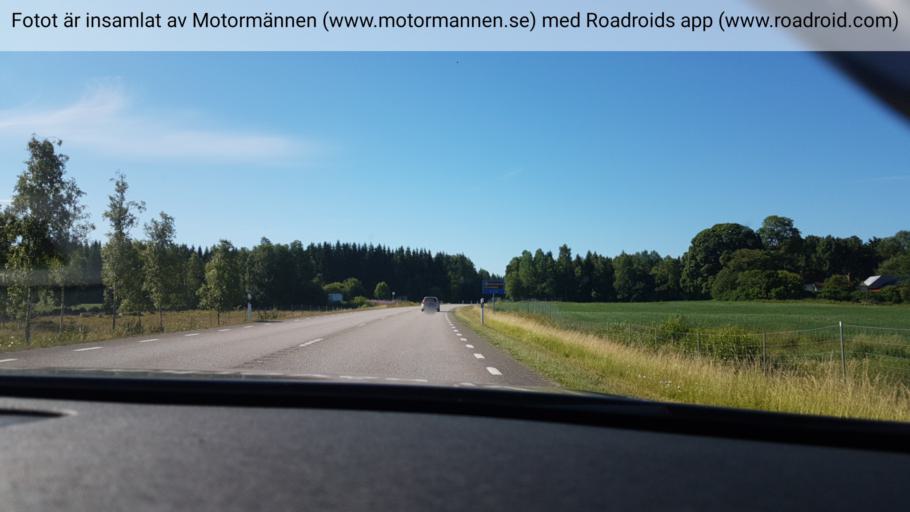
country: SE
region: Vaestra Goetaland
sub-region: Falkopings Kommun
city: Falkoeping
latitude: 58.0464
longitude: 13.5479
